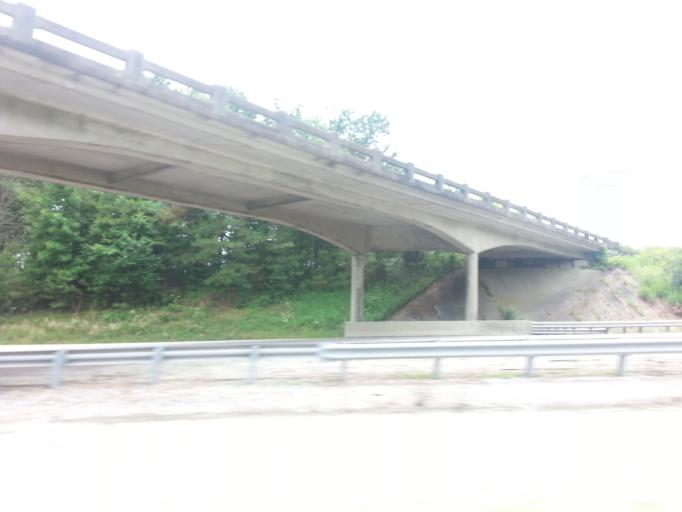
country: US
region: Tennessee
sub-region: Putnam County
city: Monterey
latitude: 36.0920
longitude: -85.2284
